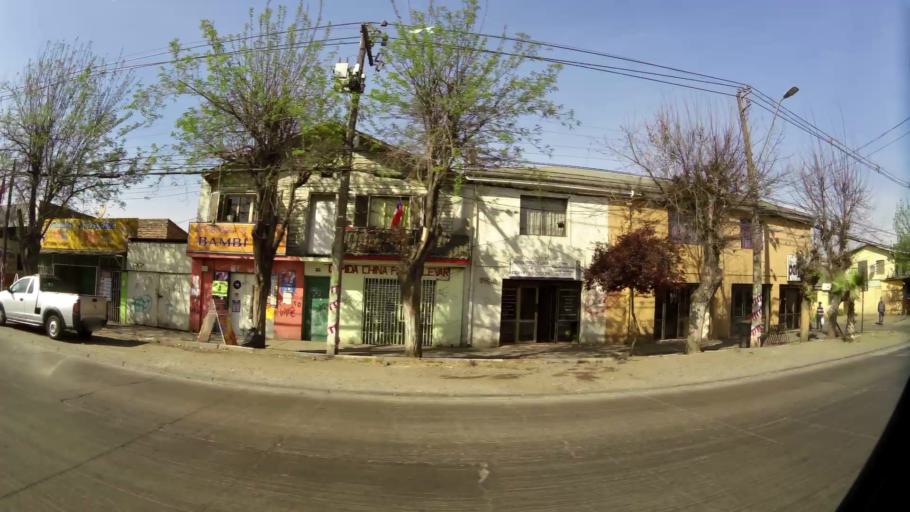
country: CL
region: Santiago Metropolitan
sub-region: Provincia de Santiago
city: Lo Prado
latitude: -33.4297
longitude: -70.7345
